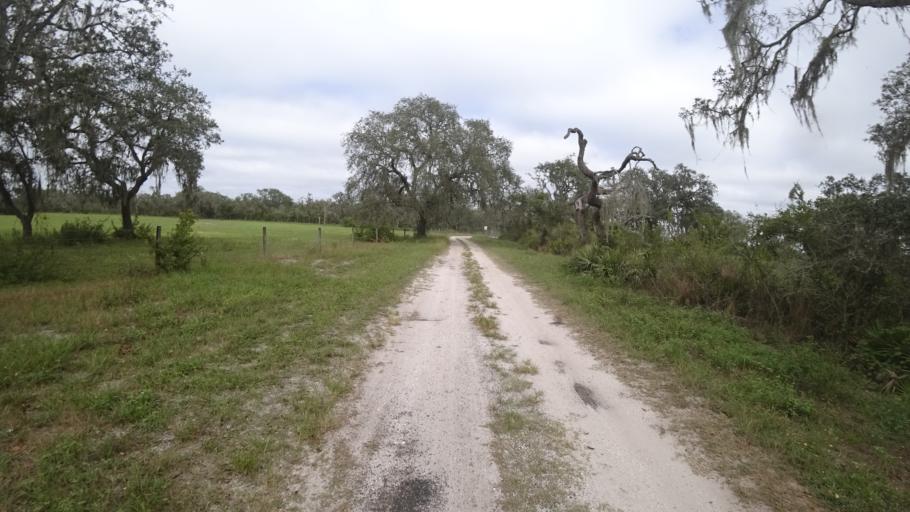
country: US
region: Florida
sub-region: Sarasota County
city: Warm Mineral Springs
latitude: 27.3237
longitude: -82.1378
